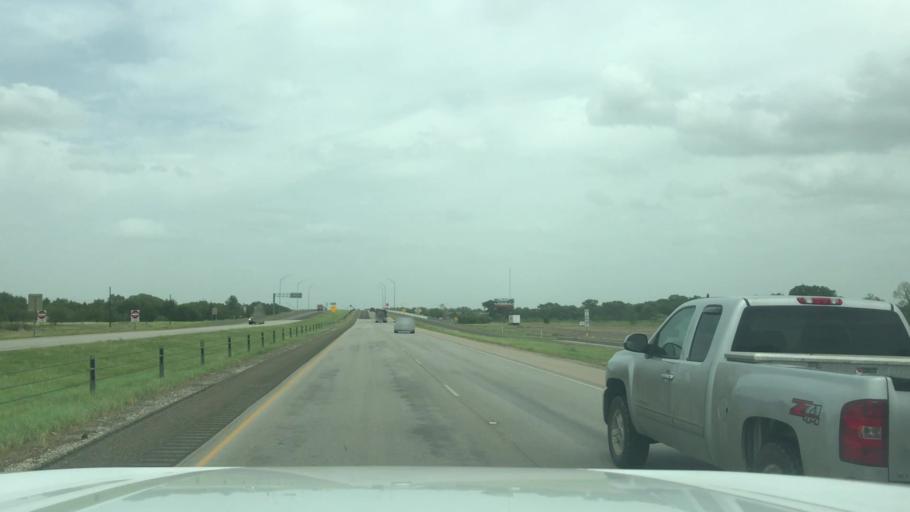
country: US
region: Texas
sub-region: McLennan County
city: Beverly
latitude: 31.5148
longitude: -97.0950
